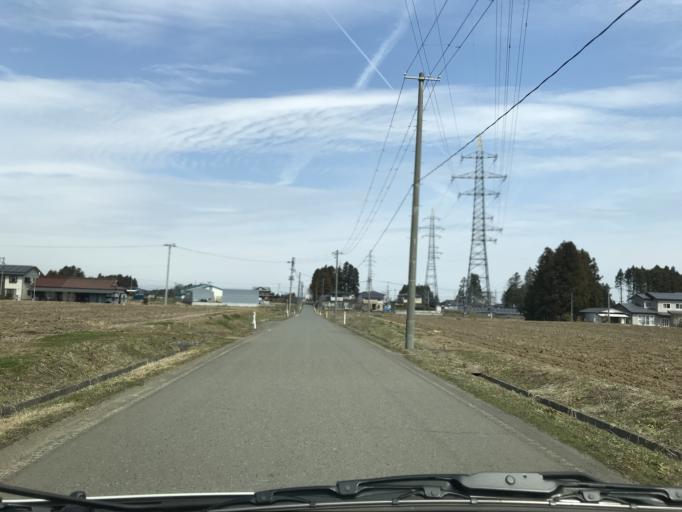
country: JP
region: Iwate
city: Mizusawa
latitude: 39.1234
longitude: 141.0855
